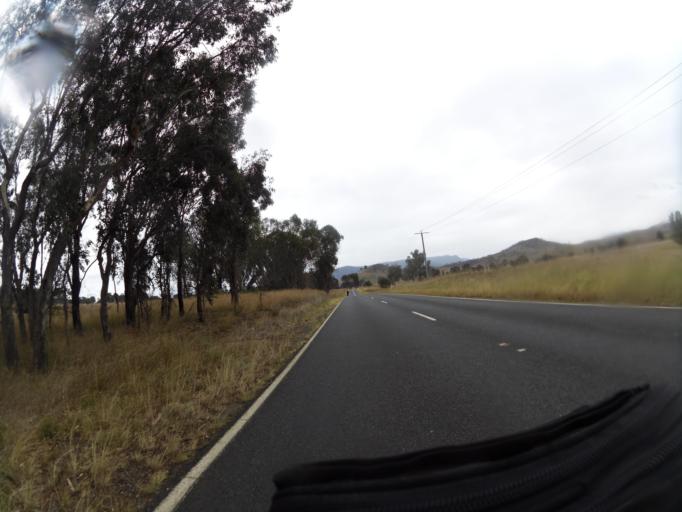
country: AU
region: New South Wales
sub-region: Greater Hume Shire
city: Holbrook
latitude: -36.2113
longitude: 147.8167
